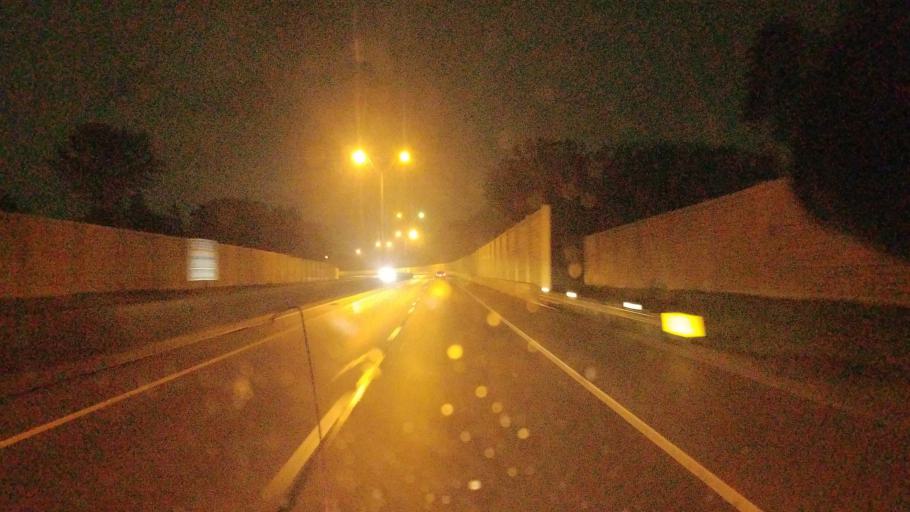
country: US
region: Ohio
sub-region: Lucas County
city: Ottawa Hills
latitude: 41.6889
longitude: -83.6585
